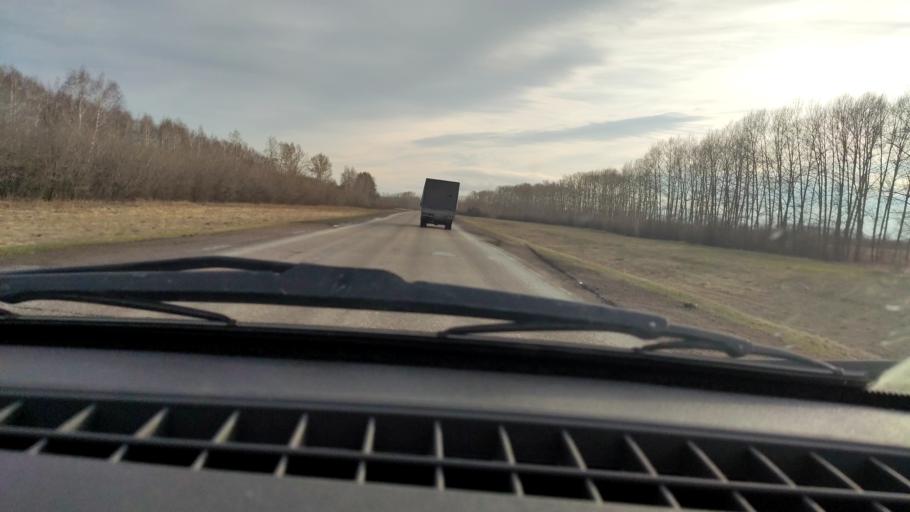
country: RU
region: Bashkortostan
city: Davlekanovo
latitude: 54.3548
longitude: 55.1850
